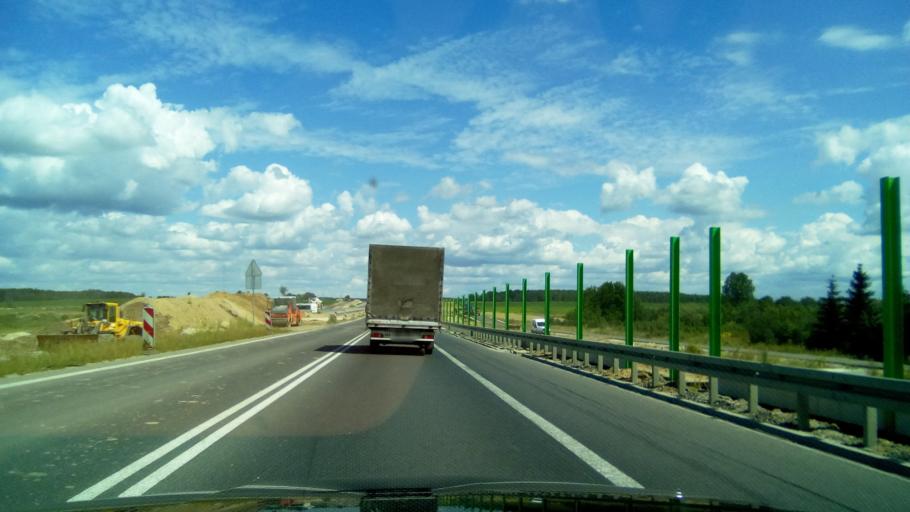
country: PL
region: Kujawsko-Pomorskie
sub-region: Powiat nakielski
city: Szubin
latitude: 52.9414
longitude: 17.7013
